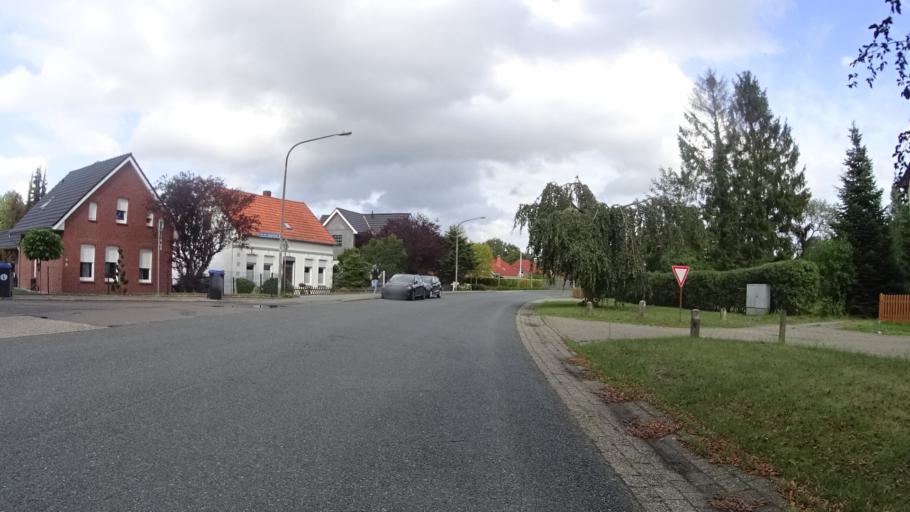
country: DE
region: Lower Saxony
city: Varel
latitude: 53.4000
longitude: 8.1150
